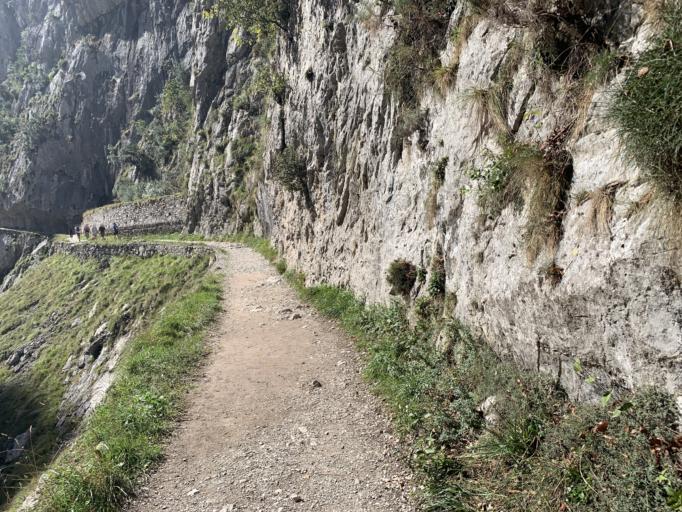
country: ES
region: Asturias
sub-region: Province of Asturias
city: Carrena
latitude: 43.2396
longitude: -4.8902
